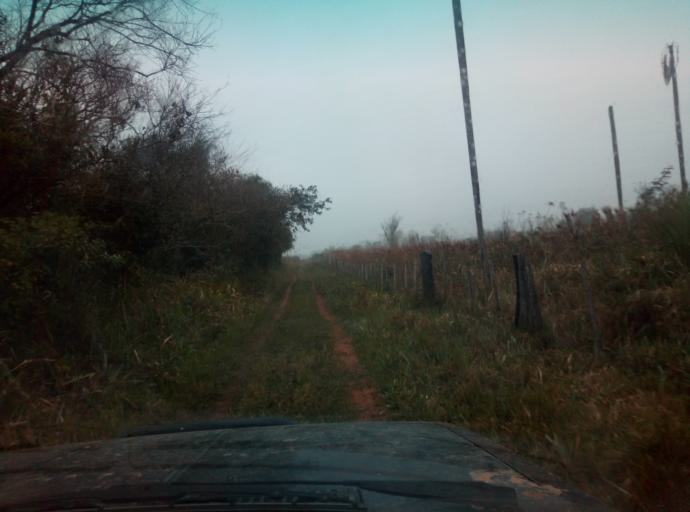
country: PY
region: Caaguazu
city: Doctor Cecilio Baez
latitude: -25.1528
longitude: -56.2609
